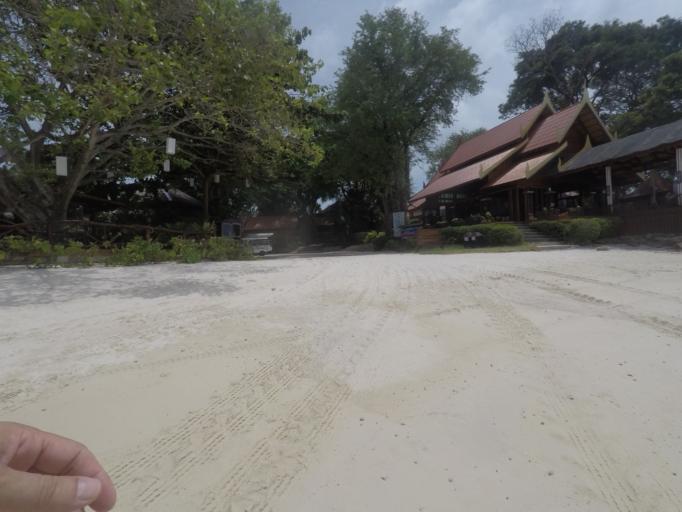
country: TH
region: Phangnga
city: Ban Phru Nai
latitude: 7.7805
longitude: 98.7618
